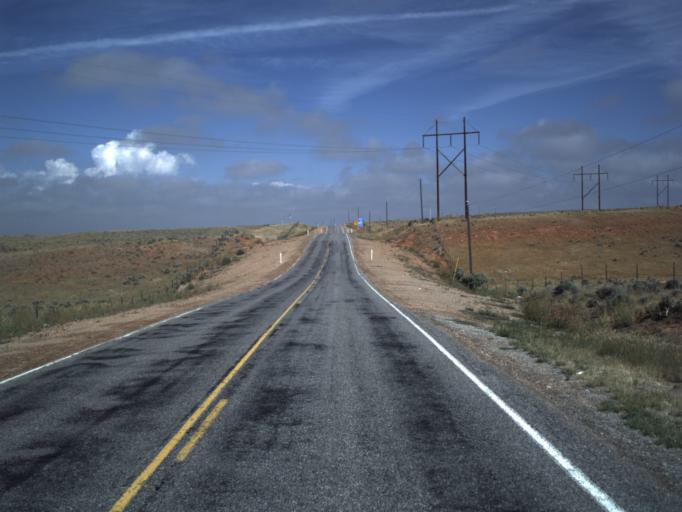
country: US
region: Wyoming
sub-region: Uinta County
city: Evanston
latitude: 41.4170
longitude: -111.0479
